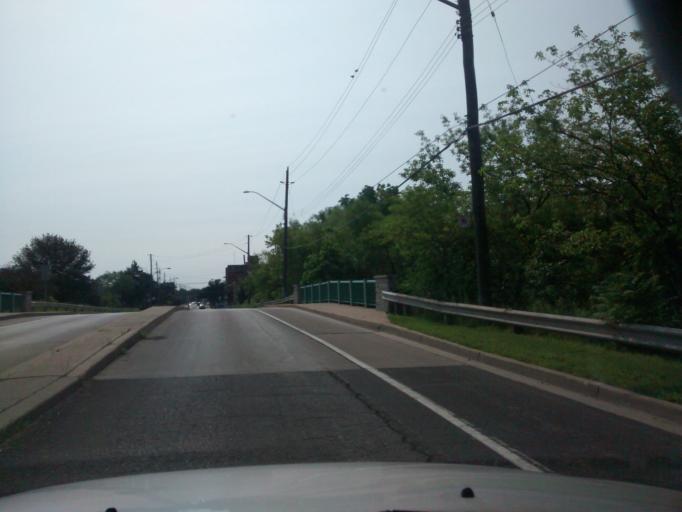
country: CA
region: Ontario
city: Hamilton
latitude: 43.2314
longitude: -79.8141
